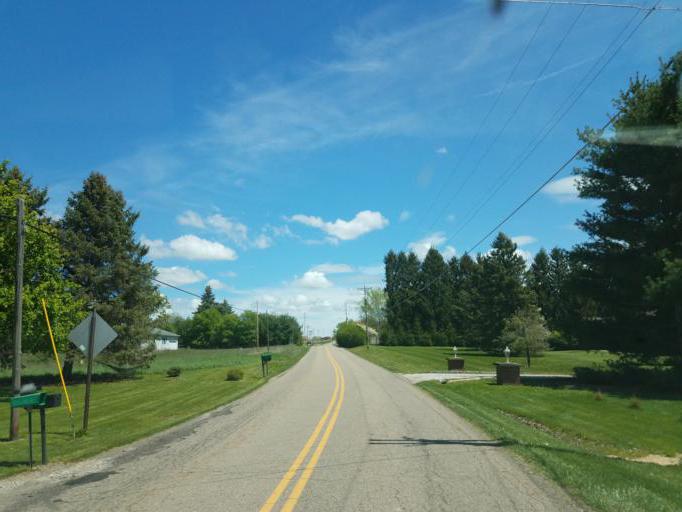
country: US
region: Ohio
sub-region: Knox County
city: Fredericktown
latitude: 40.4956
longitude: -82.4885
